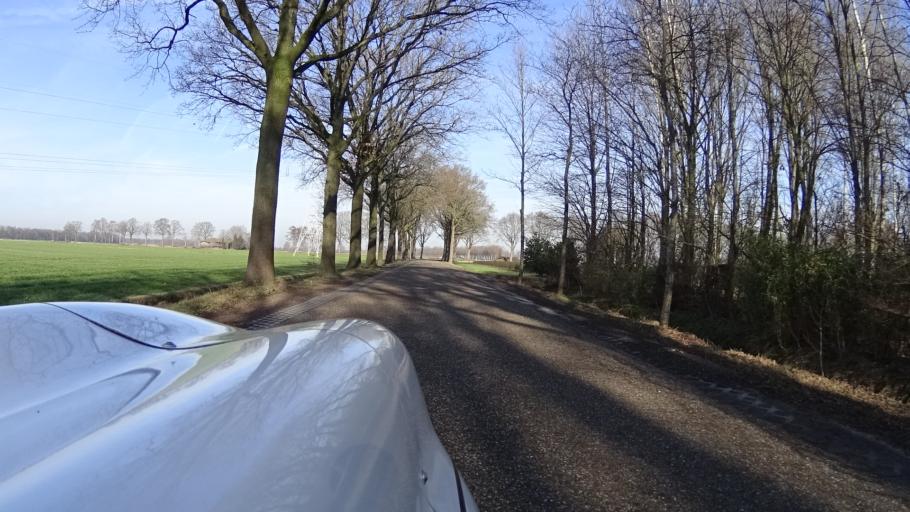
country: NL
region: North Brabant
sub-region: Gemeente Boekel
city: Boekel
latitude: 51.6044
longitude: 5.6507
